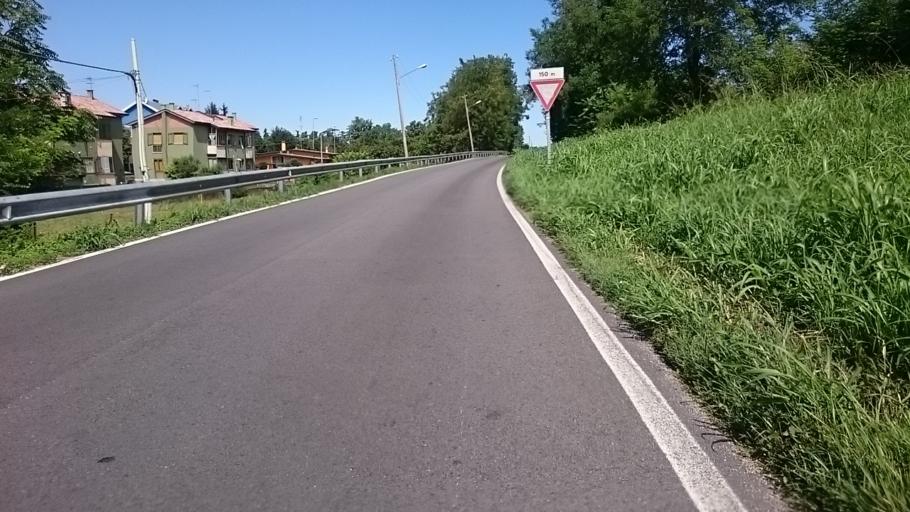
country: IT
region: Veneto
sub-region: Provincia di Padova
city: Noventa
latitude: 45.4259
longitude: 11.9526
